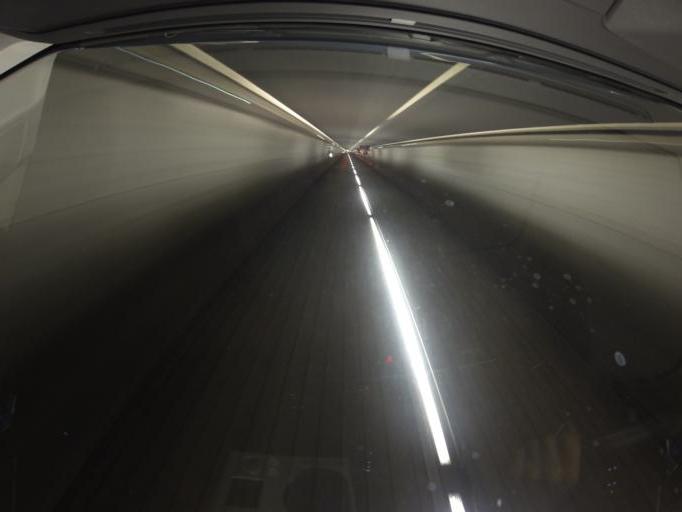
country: CH
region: Saint Gallen
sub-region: Wahlkreis See-Gaster
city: Amden
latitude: 47.1218
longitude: 9.1362
